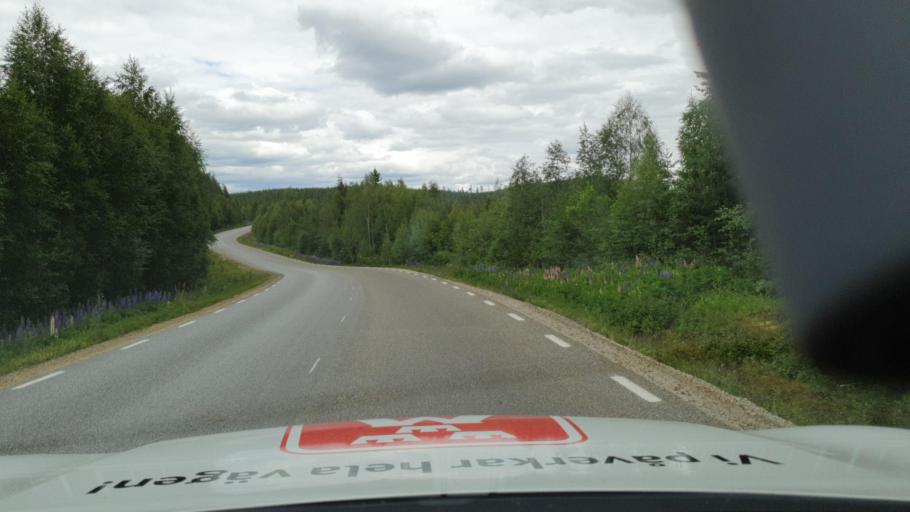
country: SE
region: Vaesterbotten
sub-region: Bjurholms Kommun
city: Bjurholm
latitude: 63.8688
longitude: 18.9731
